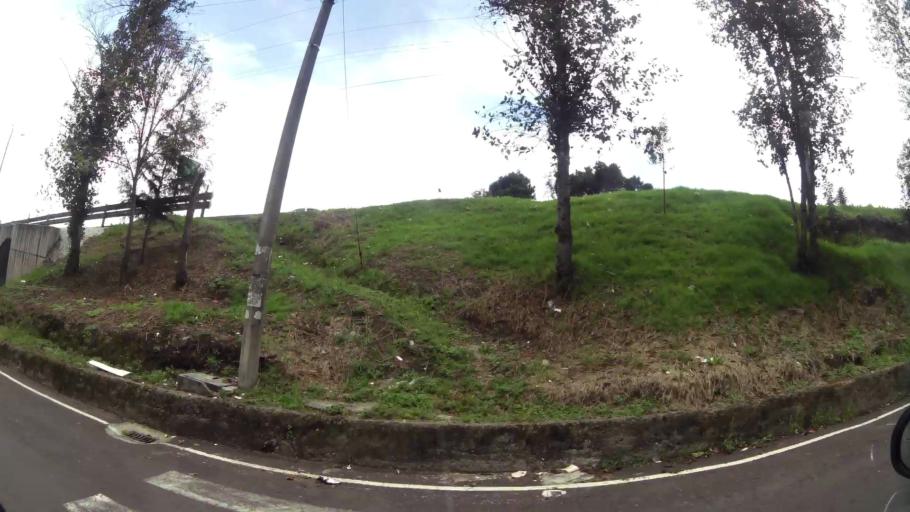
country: EC
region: Pichincha
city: Quito
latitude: -0.2415
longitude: -78.4953
